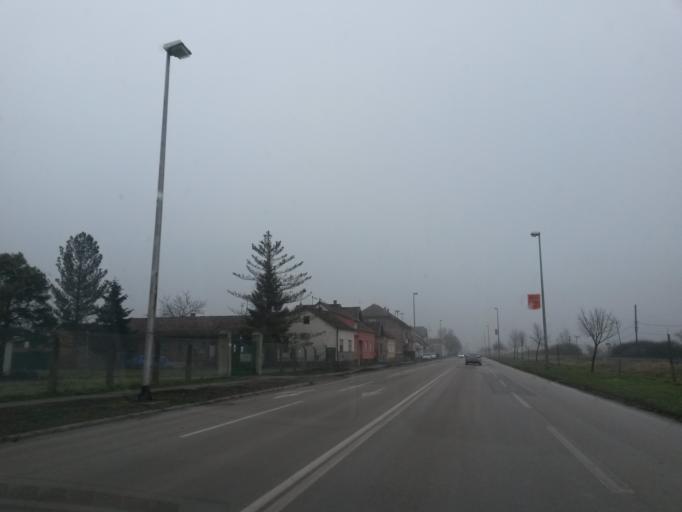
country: HR
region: Vukovarsko-Srijemska
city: Zupanja
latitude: 45.0905
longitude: 18.6969
